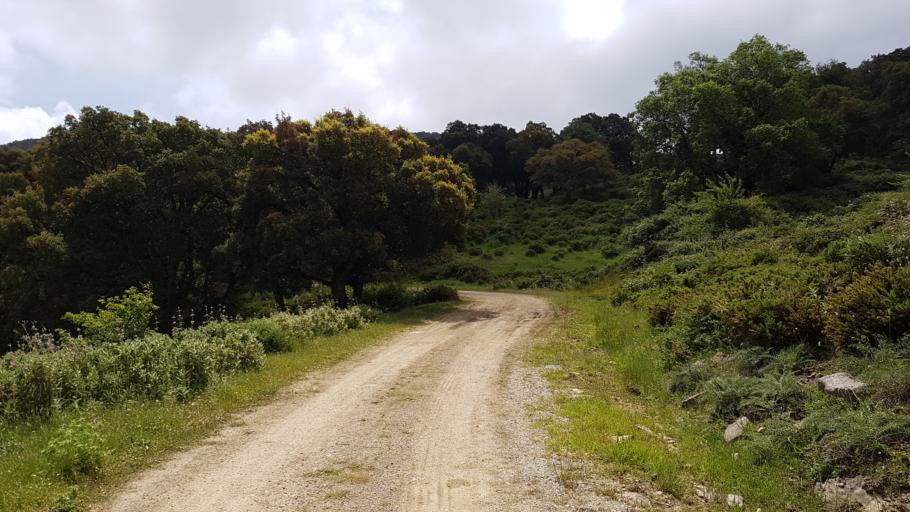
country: ES
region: Andalusia
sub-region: Provincia de Cadiz
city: Alcala de los Gazules
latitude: 36.5138
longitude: -5.5963
